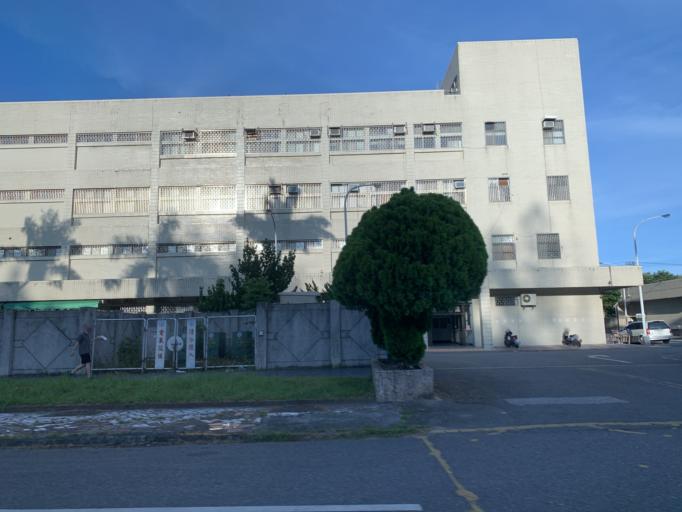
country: TW
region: Taiwan
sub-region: Hualien
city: Hualian
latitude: 24.0028
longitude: 121.6293
